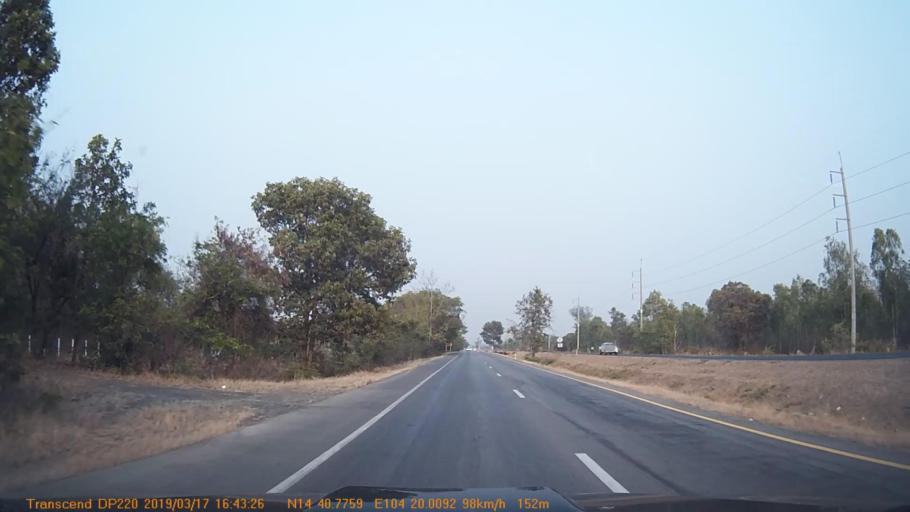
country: TH
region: Sisaket
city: Phrai Bueng
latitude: 14.6797
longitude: 104.3341
